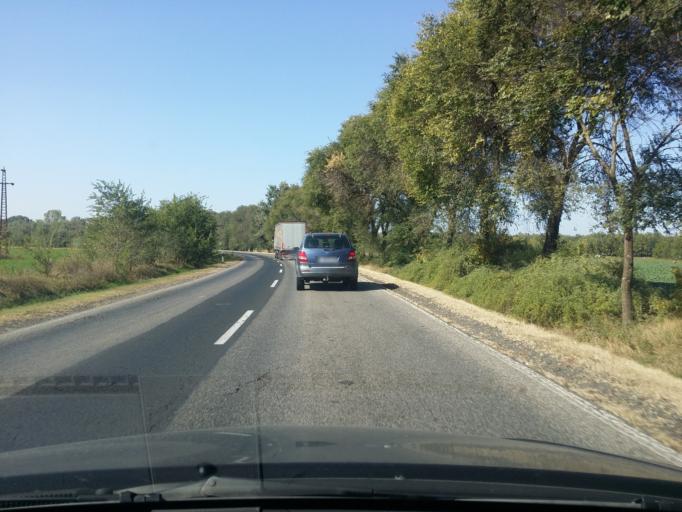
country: HU
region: Bacs-Kiskun
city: Nyarlorinc
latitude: 46.9145
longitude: 19.8005
